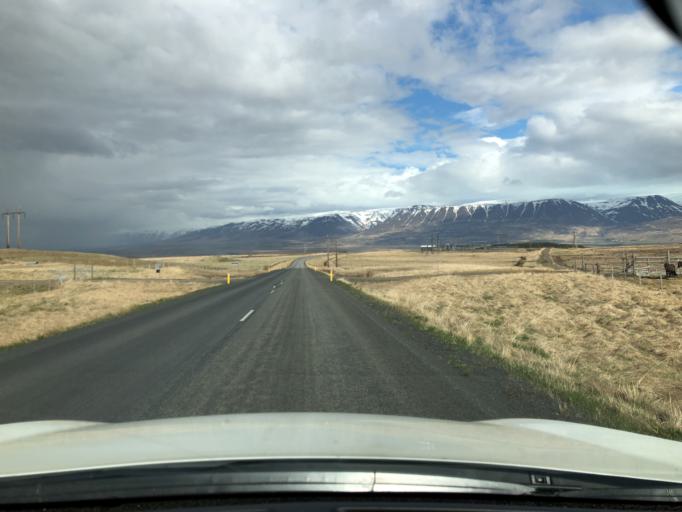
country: IS
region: Northwest
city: Saudarkrokur
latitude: 65.5445
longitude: -19.4960
